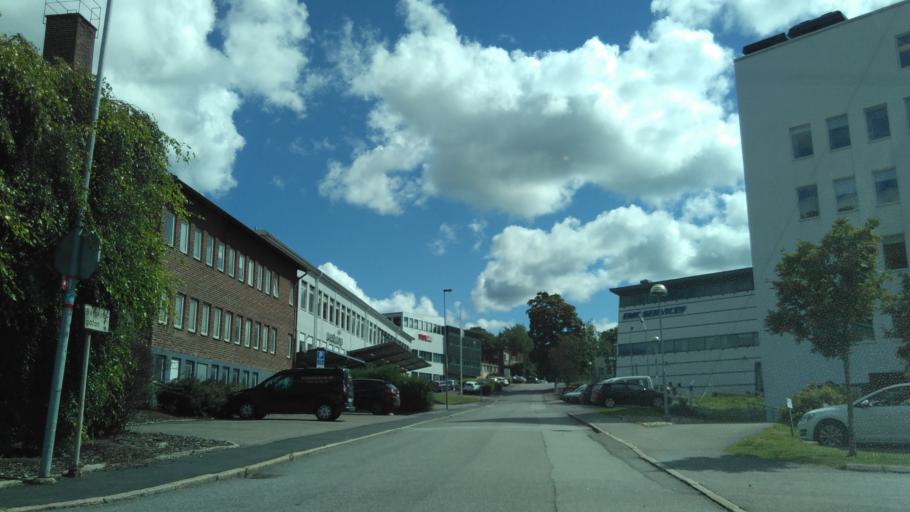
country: SE
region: Vaestra Goetaland
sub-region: Molndal
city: Moelndal
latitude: 57.6679
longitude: 12.0192
